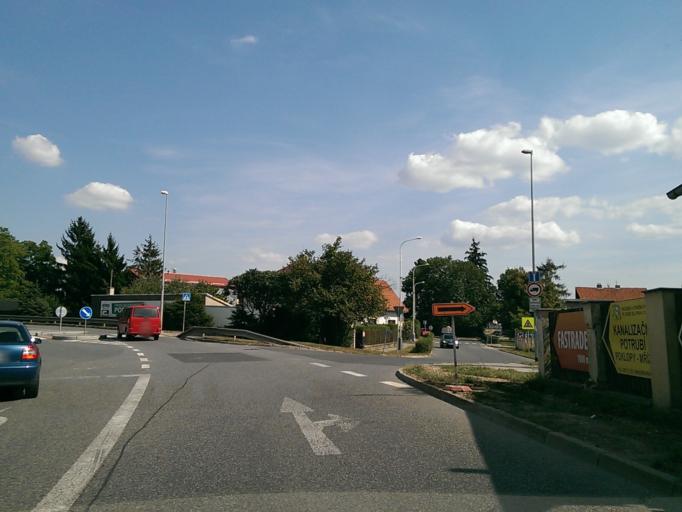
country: CZ
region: Central Bohemia
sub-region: Okres Praha-Zapad
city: Pruhonice
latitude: 50.0359
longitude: 14.5800
